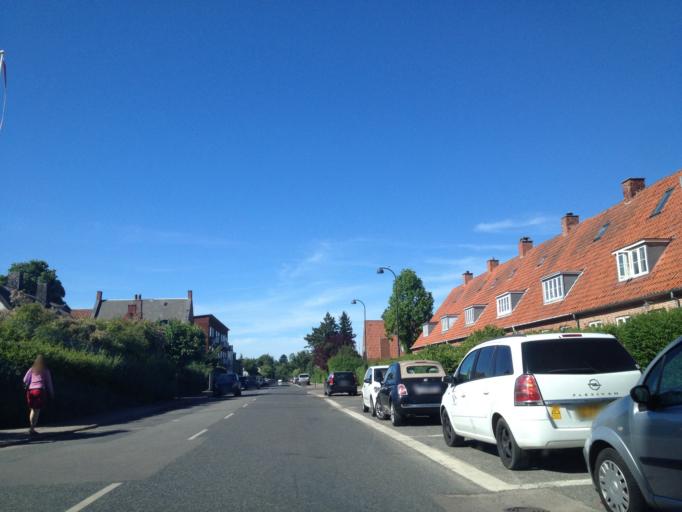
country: DK
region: Capital Region
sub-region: Gentofte Kommune
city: Charlottenlund
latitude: 55.7630
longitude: 12.5861
